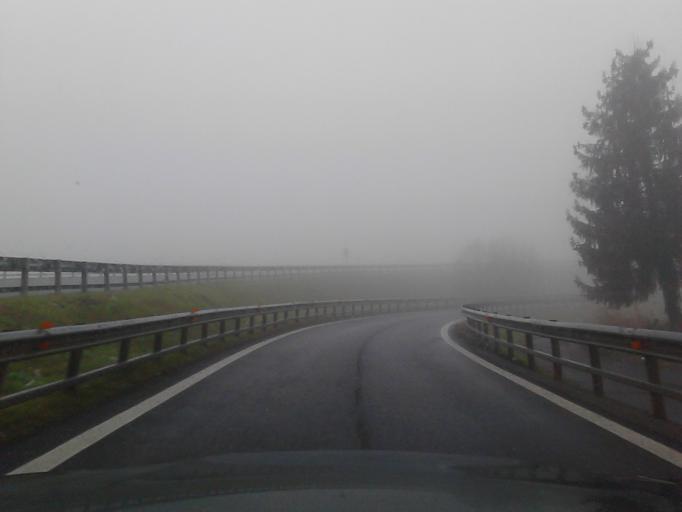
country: IT
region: Lombardy
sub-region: Provincia di Bergamo
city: Telgate
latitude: 45.6315
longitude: 9.8562
